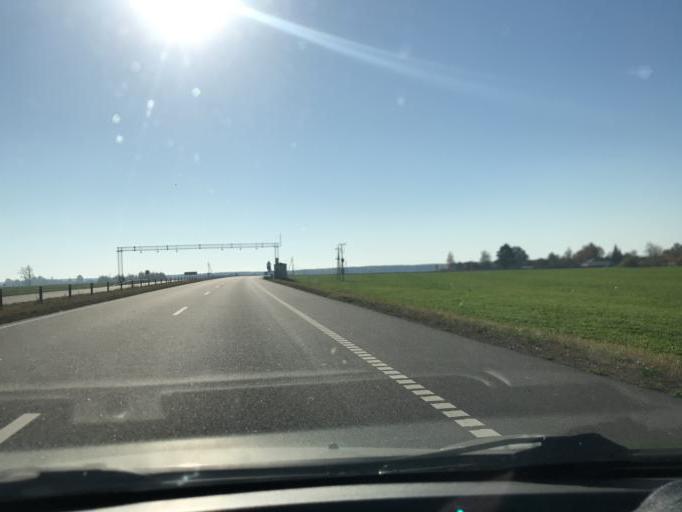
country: BY
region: Mogilev
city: Babruysk
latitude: 53.1764
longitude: 29.3591
